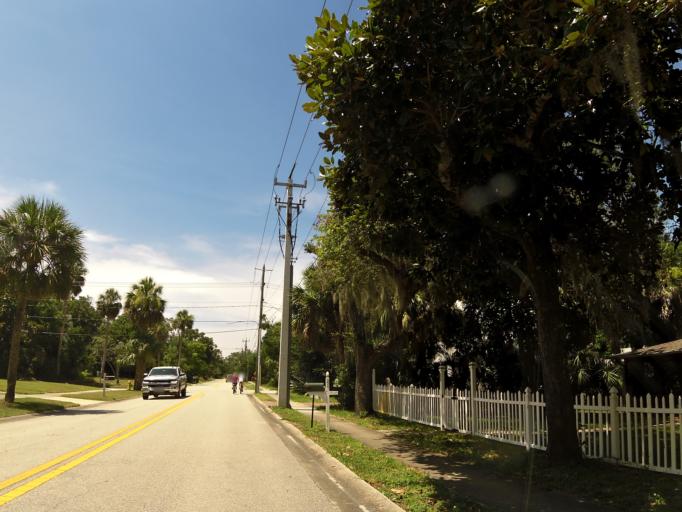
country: US
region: Florida
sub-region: Volusia County
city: Ormond Beach
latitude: 29.2859
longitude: -81.0593
